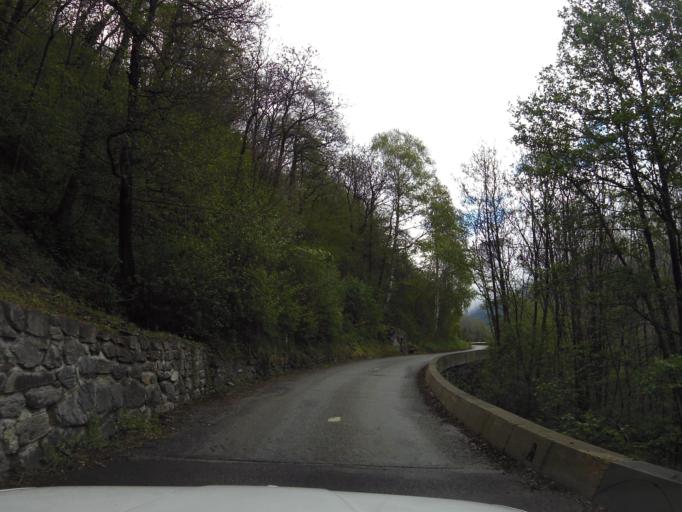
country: FR
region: Rhone-Alpes
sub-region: Departement de la Savoie
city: Saint-Michel-de-Maurienne
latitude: 45.2098
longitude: 6.5380
